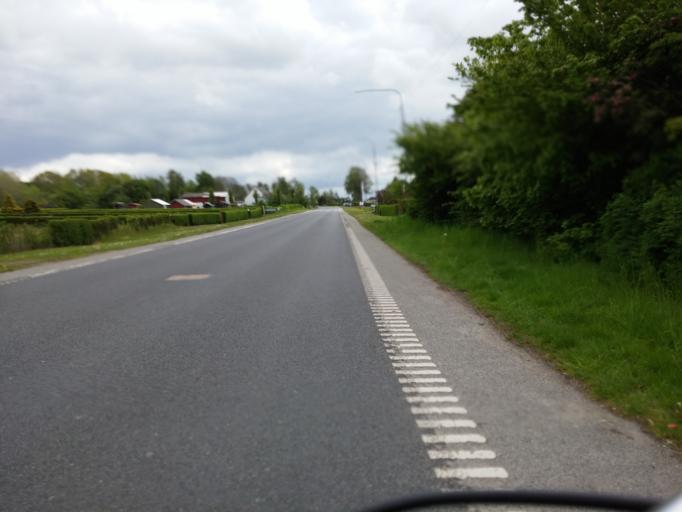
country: DK
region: South Denmark
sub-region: Kerteminde Kommune
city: Munkebo
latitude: 55.4628
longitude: 10.5465
